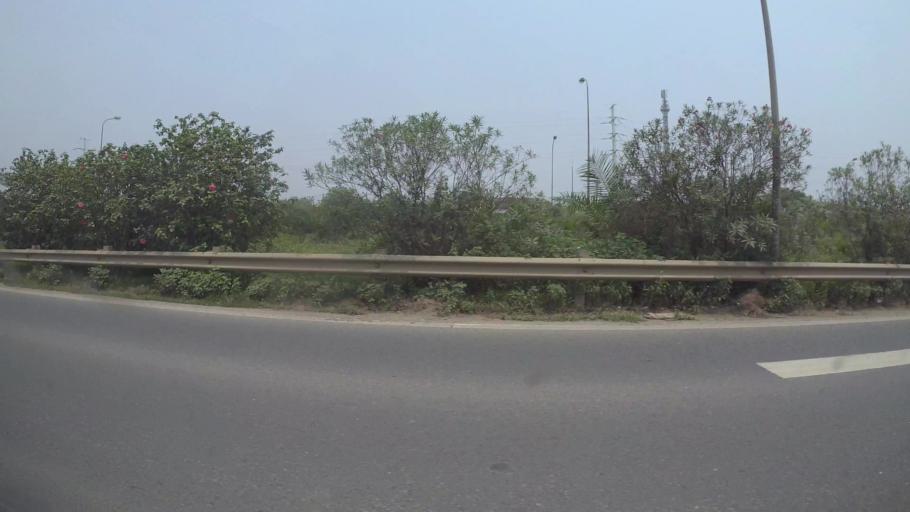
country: VN
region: Ha Noi
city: Lien Quan
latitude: 20.9903
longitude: 105.5445
